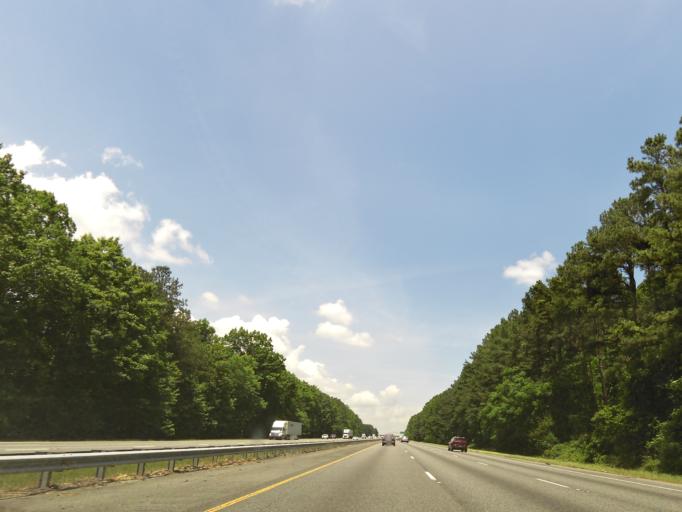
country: US
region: Georgia
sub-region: Butts County
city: Indian Springs
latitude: 33.1569
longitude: -84.0355
